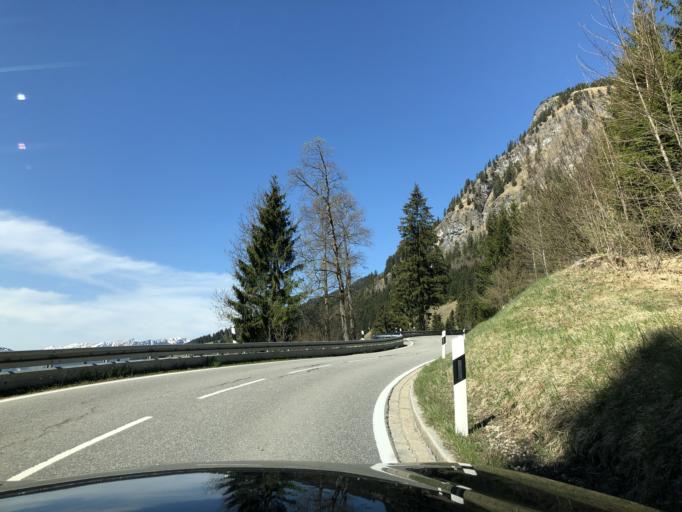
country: AT
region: Tyrol
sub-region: Politischer Bezirk Reutte
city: Schattwald
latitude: 47.5106
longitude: 10.3868
